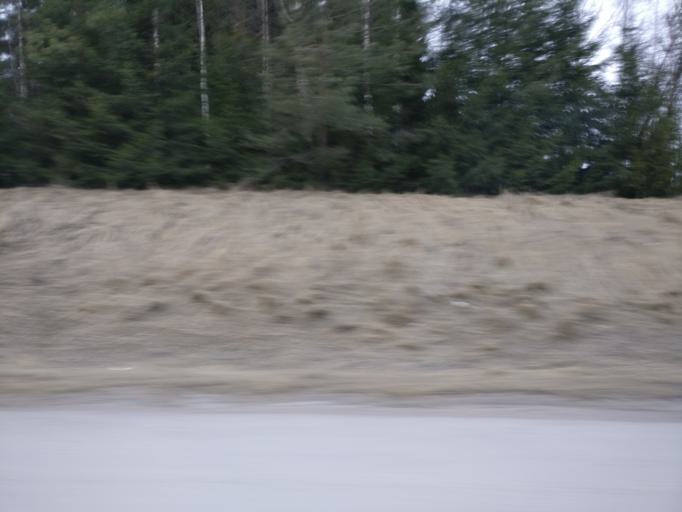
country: FI
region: Uusimaa
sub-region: Helsinki
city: Nurmijaervi
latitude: 60.5456
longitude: 24.8376
